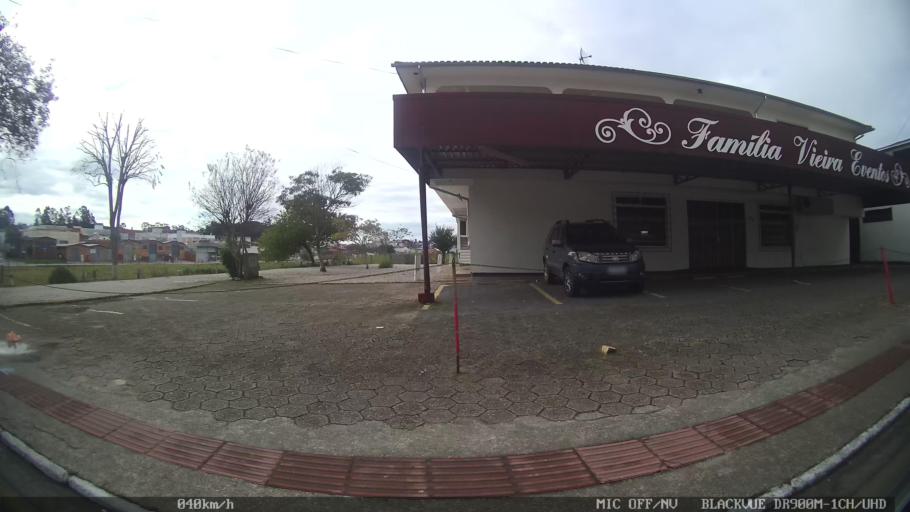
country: BR
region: Santa Catarina
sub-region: Sao Jose
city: Campinas
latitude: -27.5522
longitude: -48.6255
